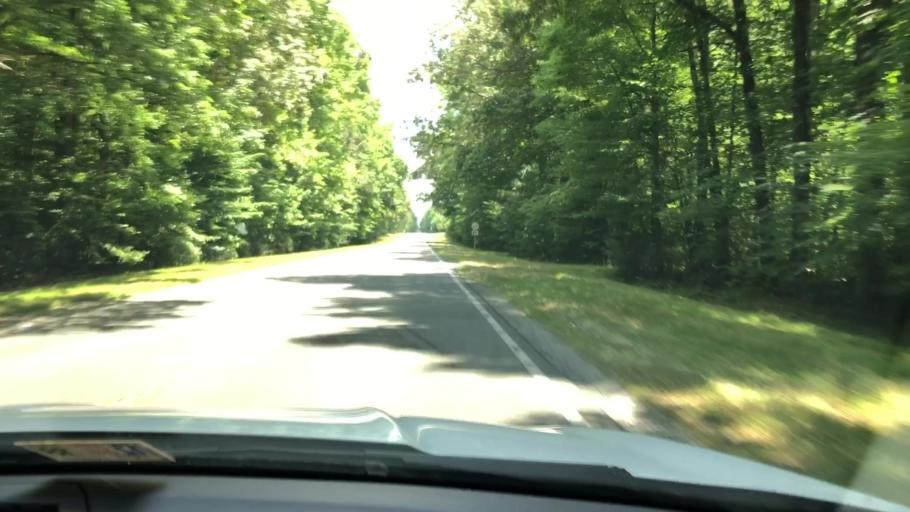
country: US
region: Virginia
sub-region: Lancaster County
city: Lancaster
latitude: 37.8126
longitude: -76.5453
